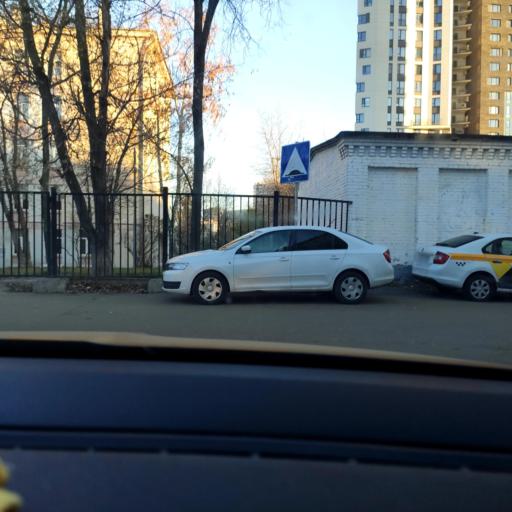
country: RU
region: Moskovskaya
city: Khoroshevo-Mnevniki
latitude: 55.7802
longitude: 37.4674
